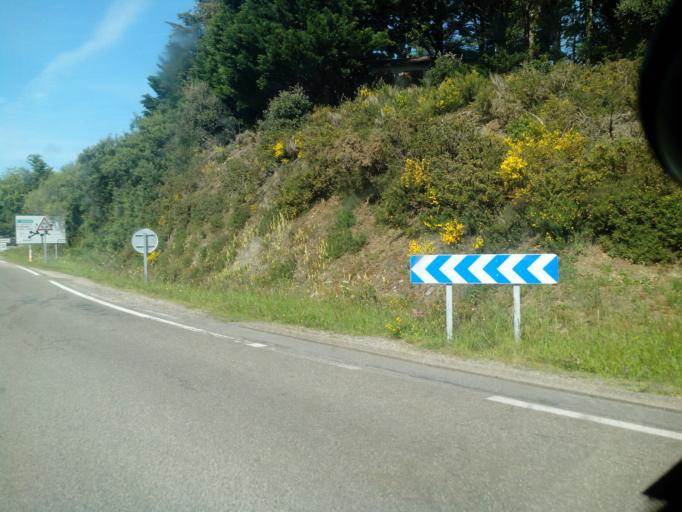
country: FR
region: Pays de la Loire
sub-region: Departement de la Loire-Atlantique
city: Pornic
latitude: 47.1114
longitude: -2.0735
